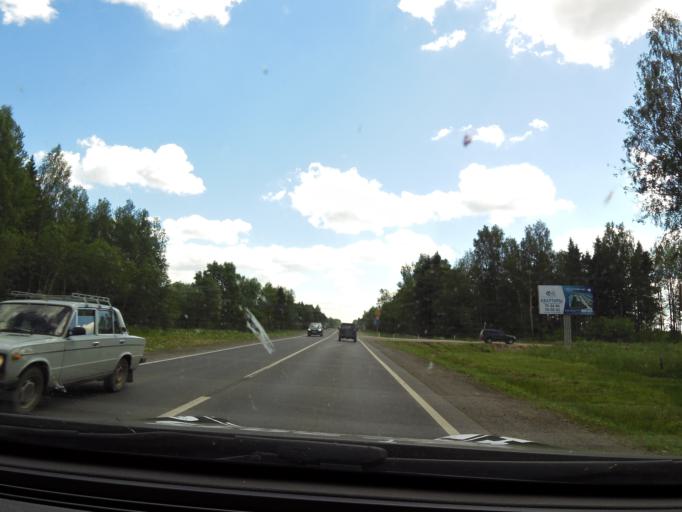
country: RU
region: Vologda
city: Molochnoye
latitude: 59.2680
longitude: 39.7327
